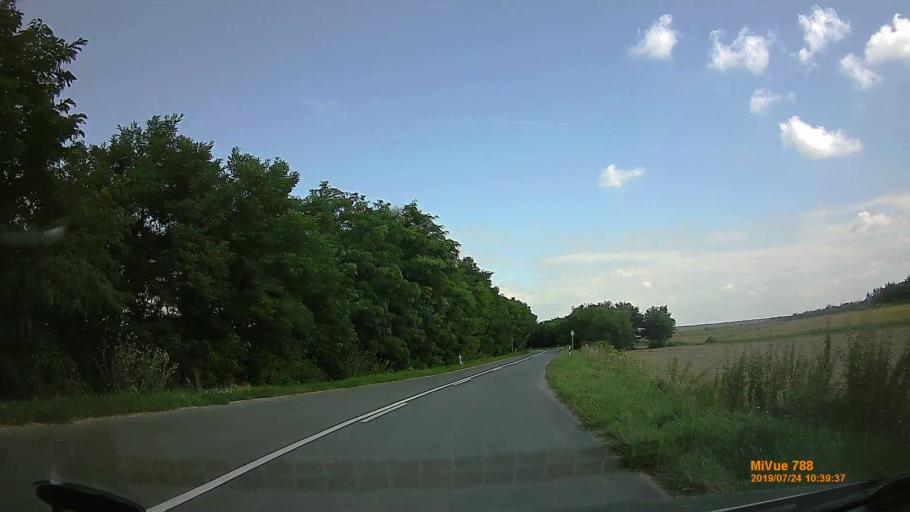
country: HU
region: Szabolcs-Szatmar-Bereg
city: Tarpa
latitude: 48.1663
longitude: 22.5429
